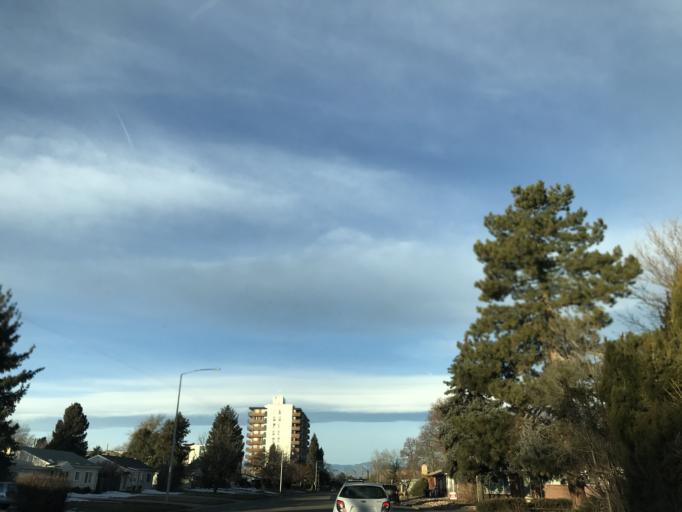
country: US
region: Colorado
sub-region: Arapahoe County
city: Glendale
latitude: 39.6675
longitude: -104.9320
